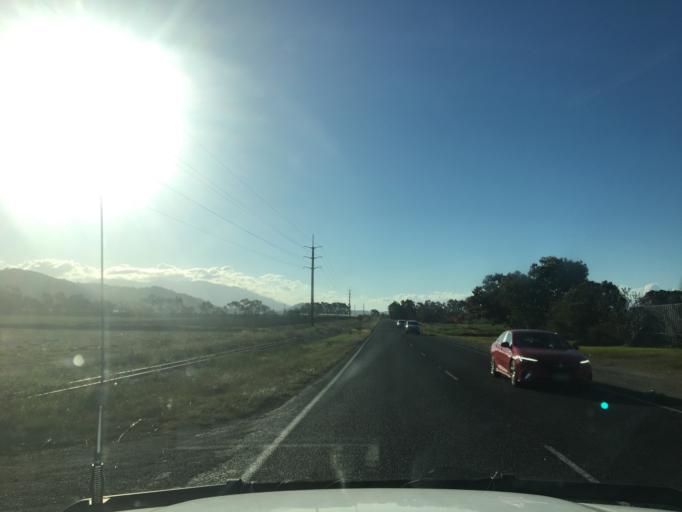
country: AU
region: Queensland
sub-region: Cairns
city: Port Douglas
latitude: -16.5132
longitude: 145.4449
